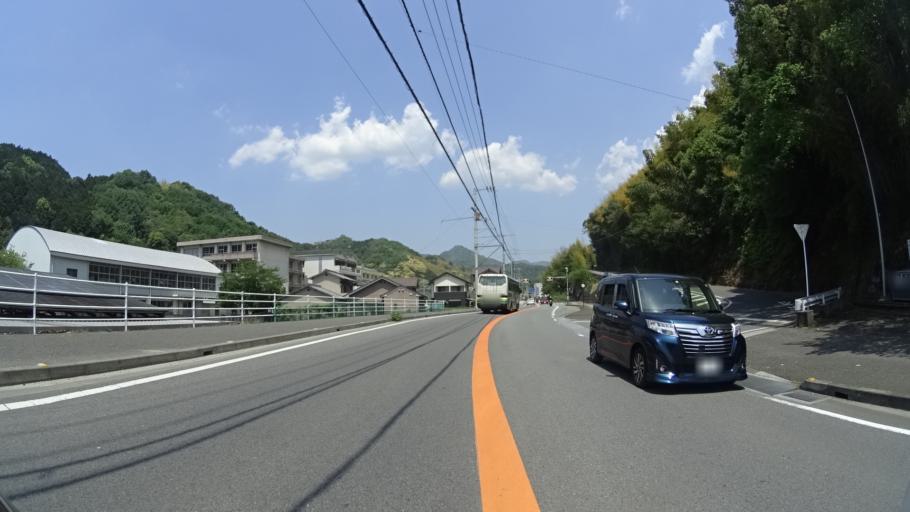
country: JP
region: Ehime
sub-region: Shikoku-chuo Shi
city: Matsuyama
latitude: 33.8594
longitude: 132.8136
